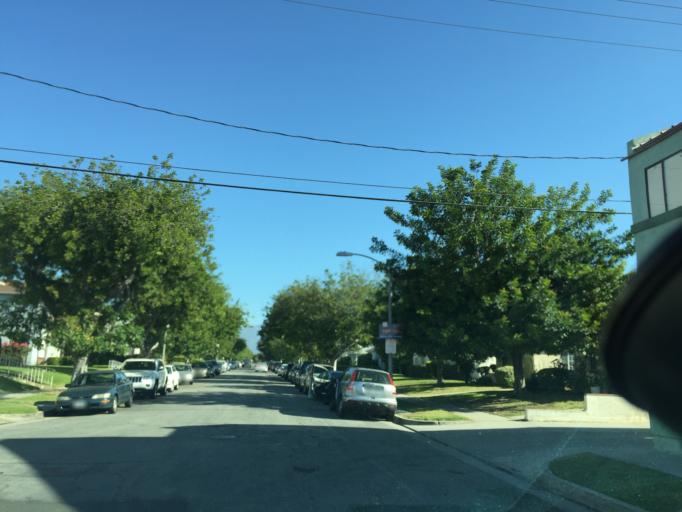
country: US
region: California
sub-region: Los Angeles County
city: Monterey Park
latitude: 34.0788
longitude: -118.1243
